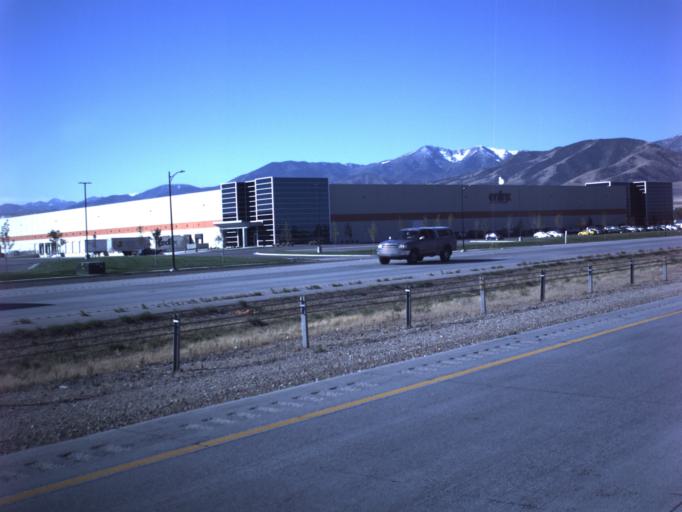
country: US
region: Utah
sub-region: Salt Lake County
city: Magna
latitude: 40.7191
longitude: -112.0558
